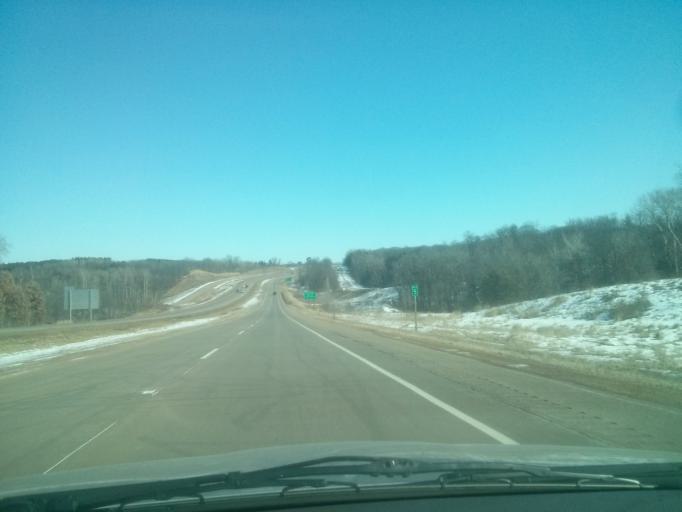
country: US
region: Wisconsin
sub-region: Saint Croix County
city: Somerset
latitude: 45.0983
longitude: -92.7336
